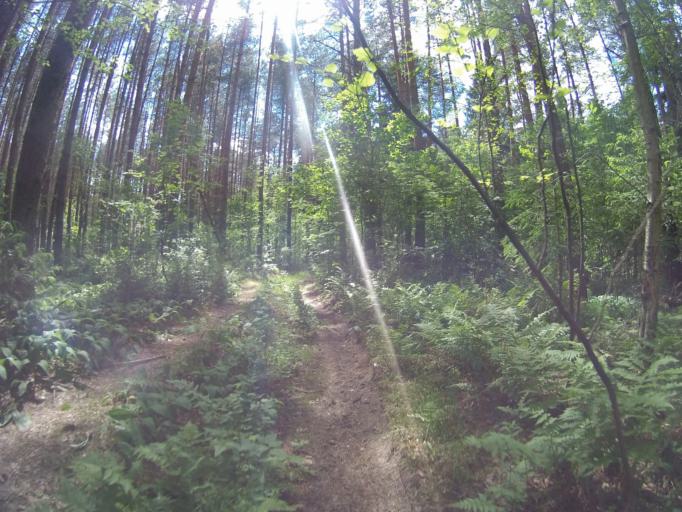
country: RU
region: Vladimir
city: Raduzhnyy
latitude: 56.0193
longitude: 40.2907
